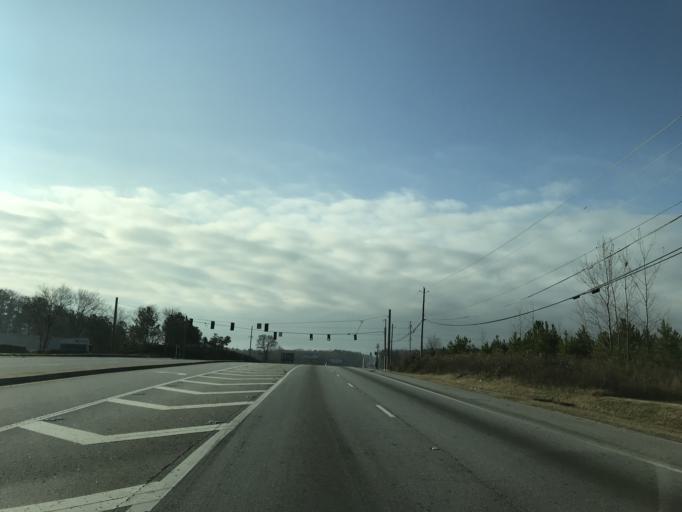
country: US
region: Georgia
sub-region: Clayton County
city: Forest Park
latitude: 33.6104
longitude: -84.4031
